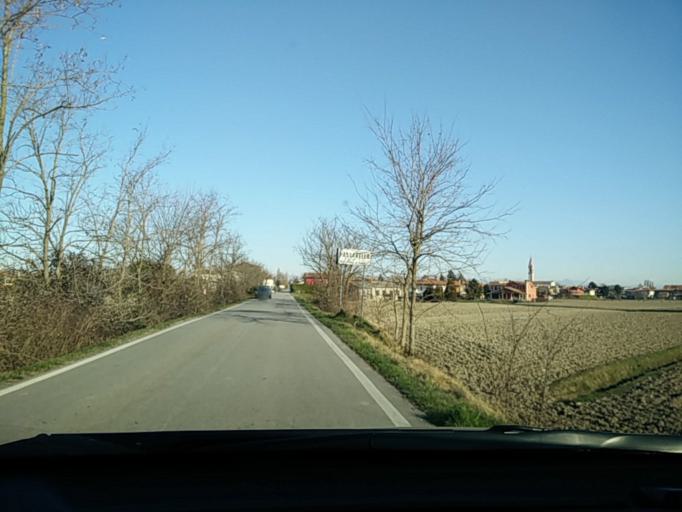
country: IT
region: Veneto
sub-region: Provincia di Venezia
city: Passarella
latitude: 45.5892
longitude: 12.6068
